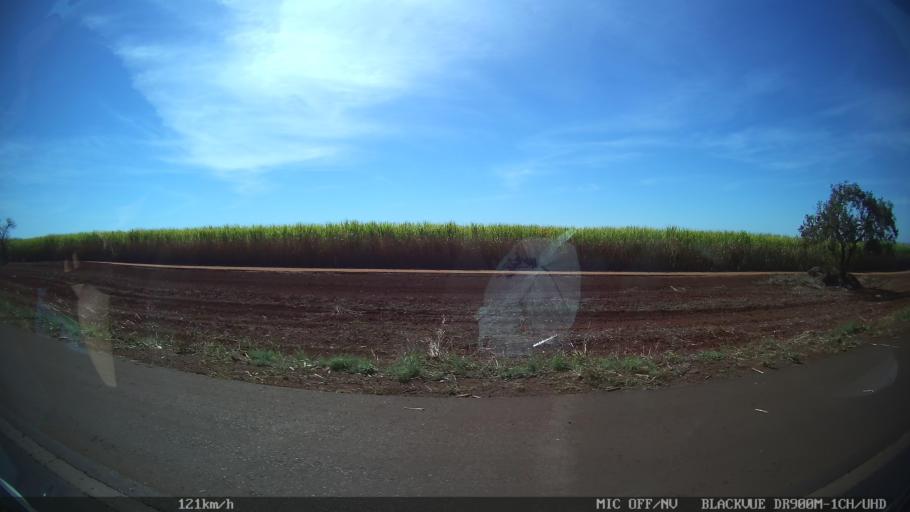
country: BR
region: Sao Paulo
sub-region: Ipua
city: Ipua
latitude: -20.4998
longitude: -47.9558
